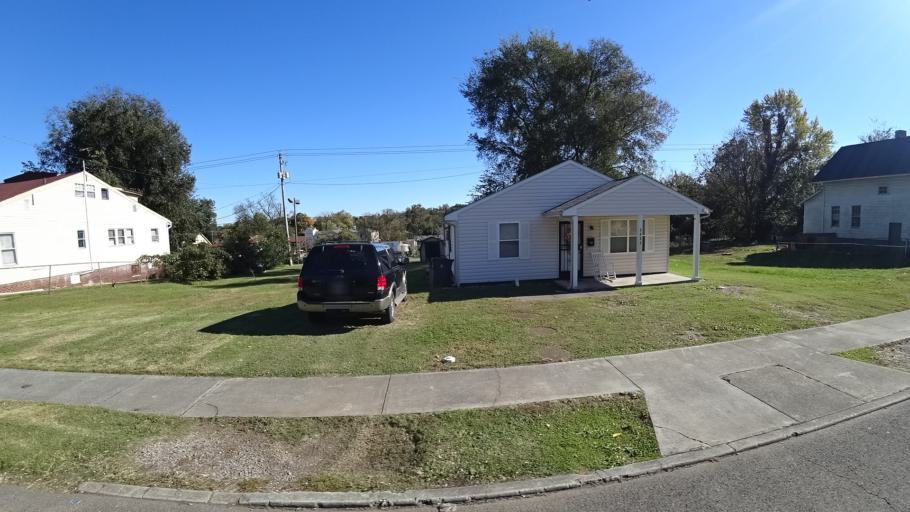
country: US
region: Tennessee
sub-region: Knox County
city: Knoxville
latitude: 35.9825
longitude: -83.8957
